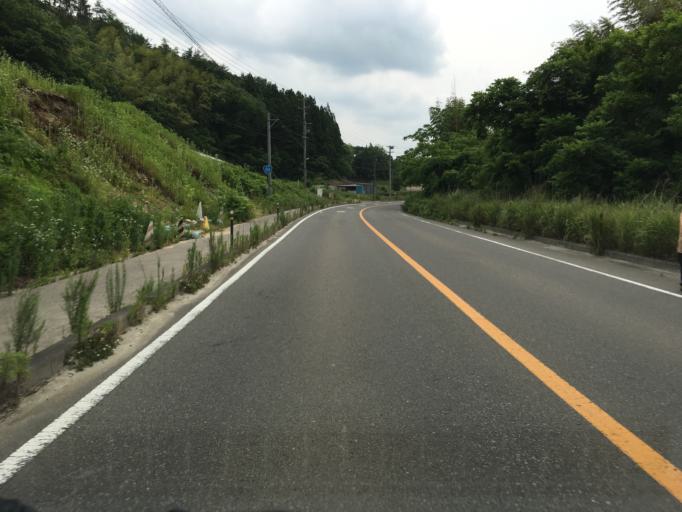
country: JP
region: Fukushima
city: Hobaramachi
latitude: 37.6839
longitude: 140.6182
